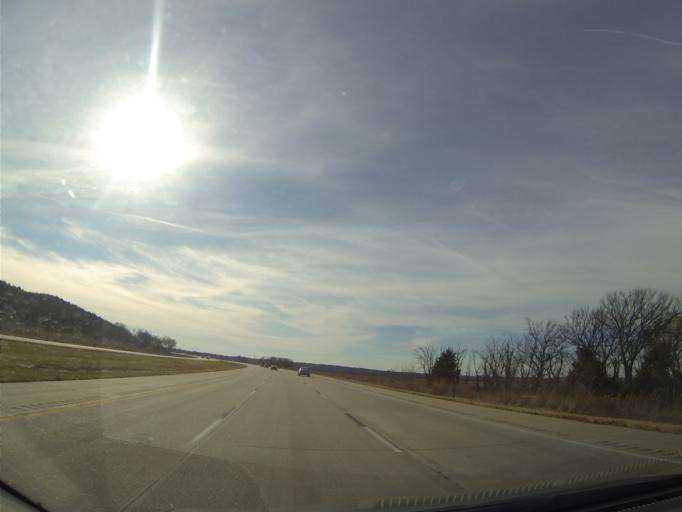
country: US
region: Nebraska
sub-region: Saunders County
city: Ashland
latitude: 41.0591
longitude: -96.2957
